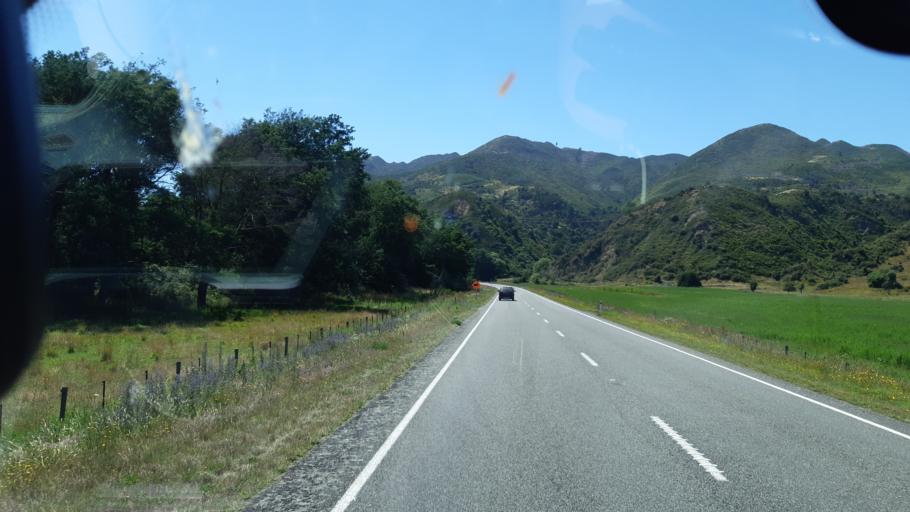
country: NZ
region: Canterbury
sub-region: Kaikoura District
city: Kaikoura
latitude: -42.6368
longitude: 173.3379
